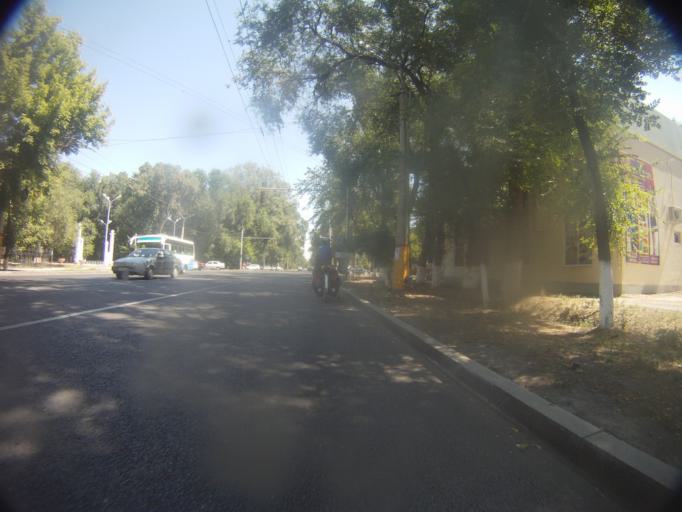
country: KZ
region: Zhambyl
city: Taraz
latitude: 42.9014
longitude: 71.3341
